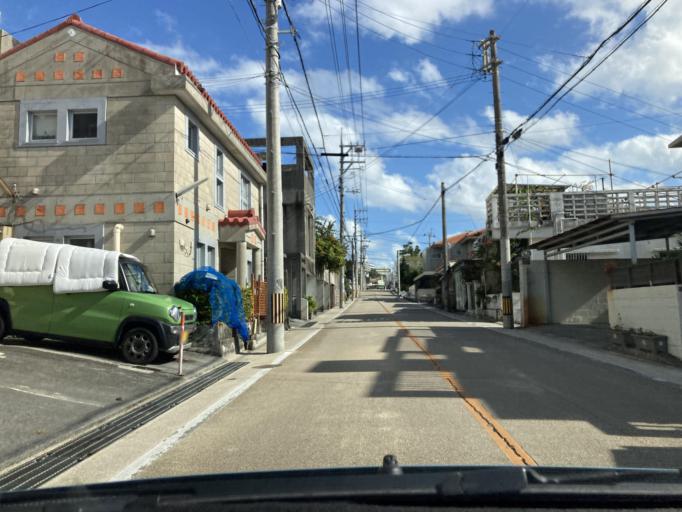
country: JP
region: Okinawa
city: Naha-shi
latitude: 26.2180
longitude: 127.7104
